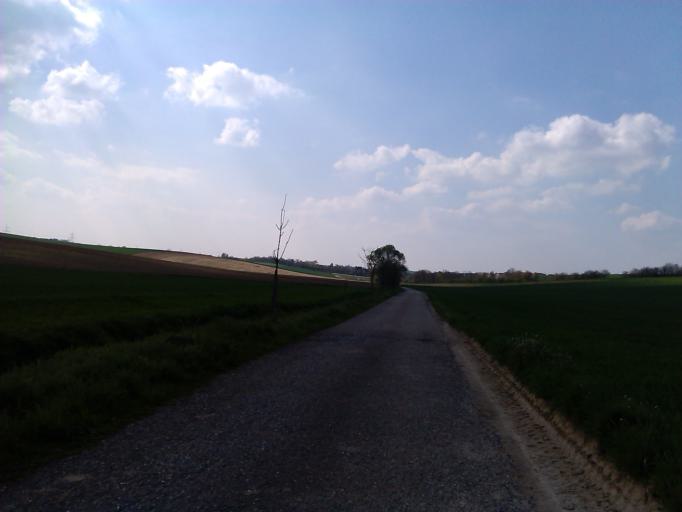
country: DE
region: Baden-Wuerttemberg
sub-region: Regierungsbezirk Stuttgart
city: Gemmingen
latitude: 49.1424
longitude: 8.9857
